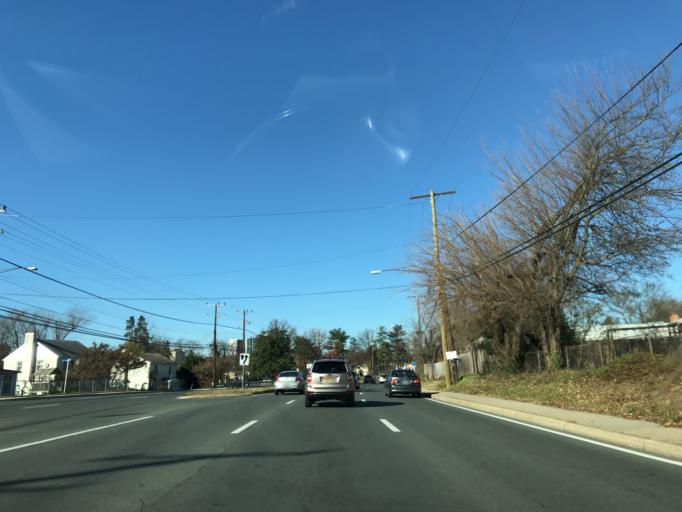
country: US
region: Maryland
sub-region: Montgomery County
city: Wheaton
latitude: 39.0364
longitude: -77.0377
